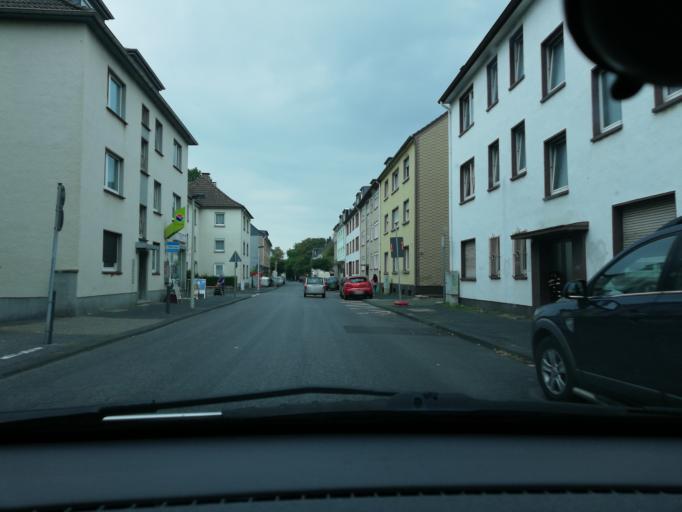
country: DE
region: North Rhine-Westphalia
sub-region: Regierungsbezirk Dusseldorf
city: Solingen
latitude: 51.1724
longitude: 7.0912
